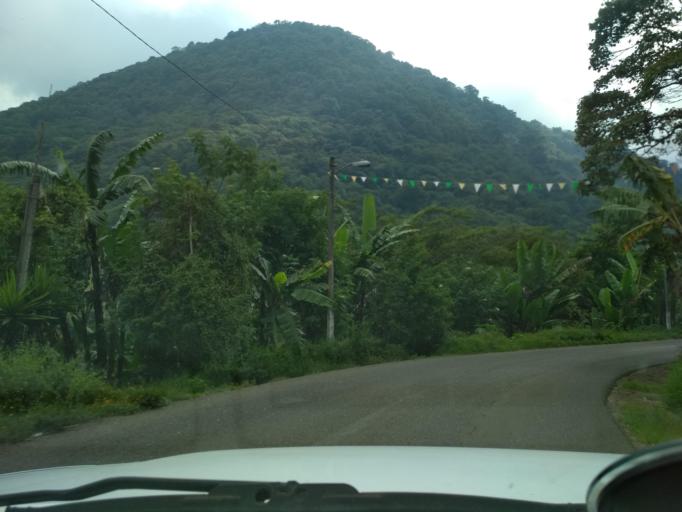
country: MX
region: Veracruz
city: Tocuila
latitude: 18.9465
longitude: -97.0319
